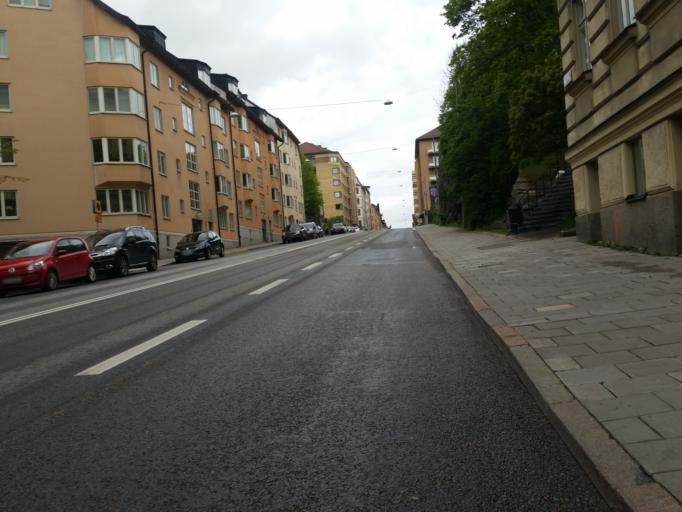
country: SE
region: Stockholm
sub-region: Stockholms Kommun
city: OEstermalm
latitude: 59.3117
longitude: 18.0857
